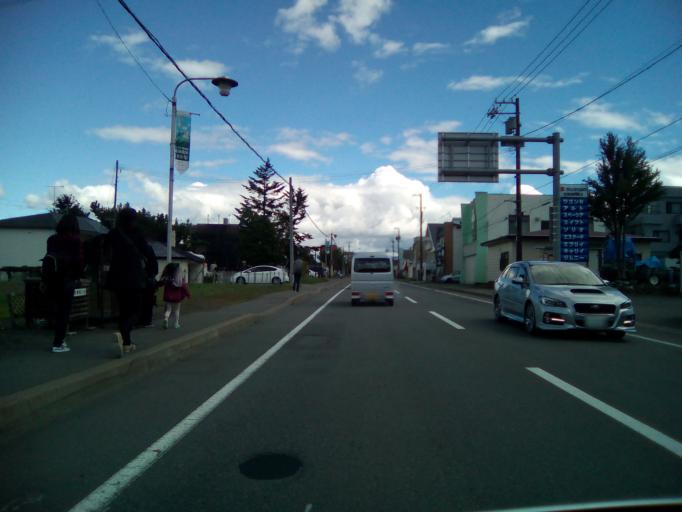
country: JP
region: Hokkaido
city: Date
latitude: 42.5651
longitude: 140.8136
